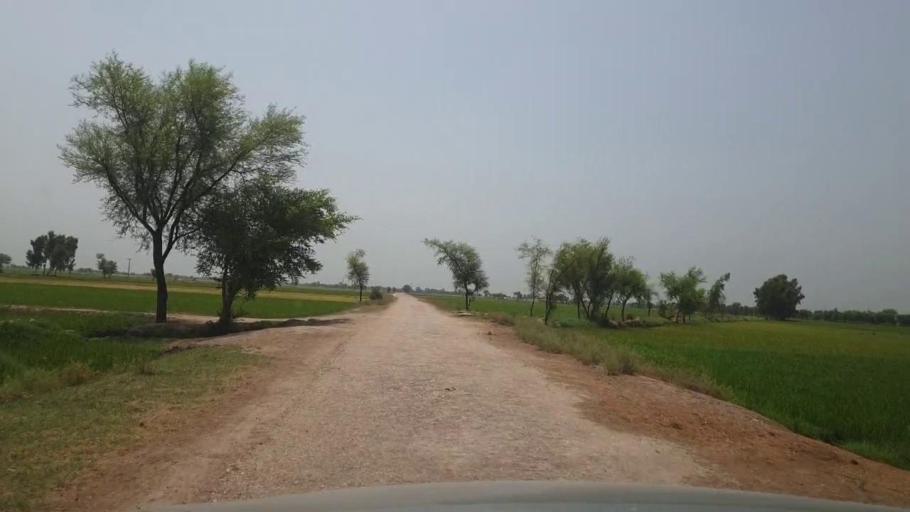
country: PK
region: Sindh
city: Garhi Yasin
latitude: 27.9209
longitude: 68.4040
